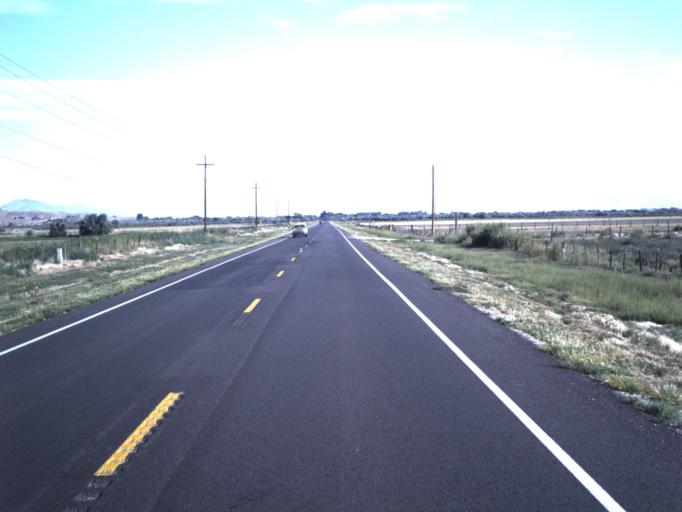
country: US
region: Utah
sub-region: Sevier County
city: Salina
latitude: 38.9761
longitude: -111.8604
